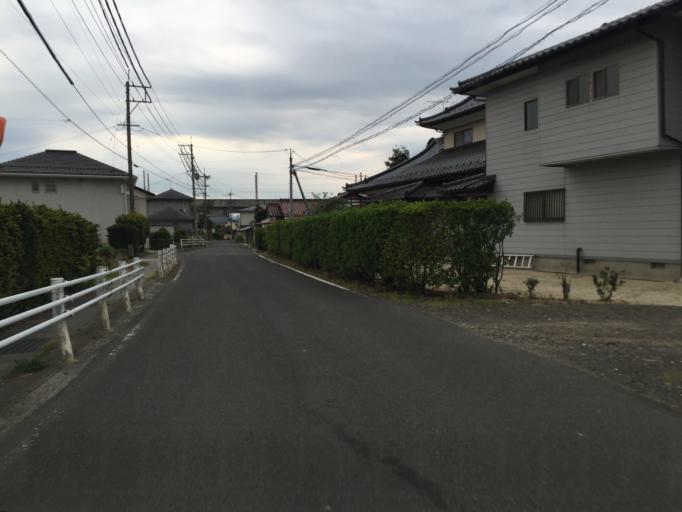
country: JP
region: Fukushima
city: Fukushima-shi
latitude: 37.8077
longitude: 140.4799
